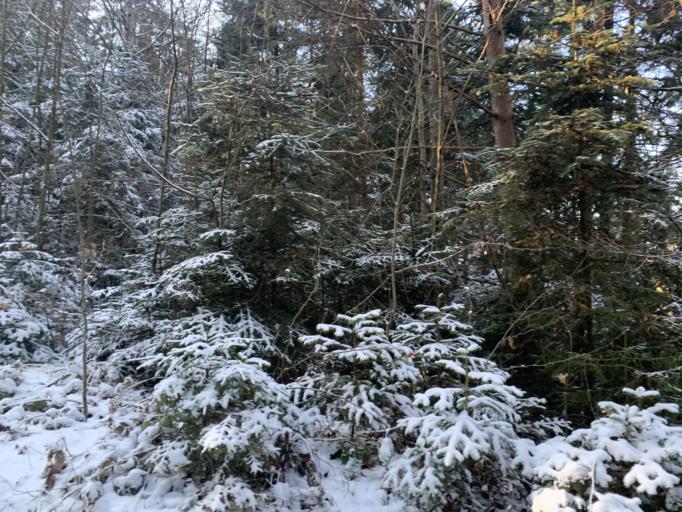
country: GE
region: Shida Kartli
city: Gori
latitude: 41.8730
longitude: 44.0298
